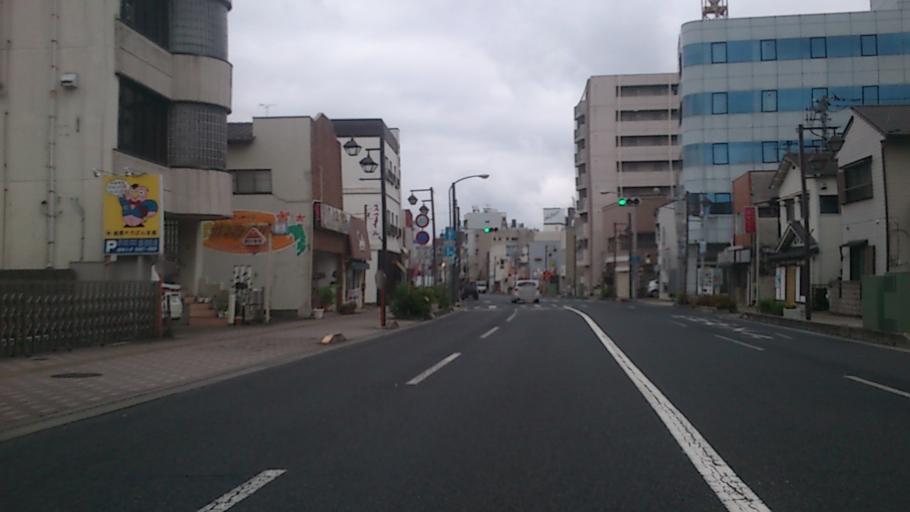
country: JP
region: Ibaraki
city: Mito-shi
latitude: 36.3843
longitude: 140.4574
